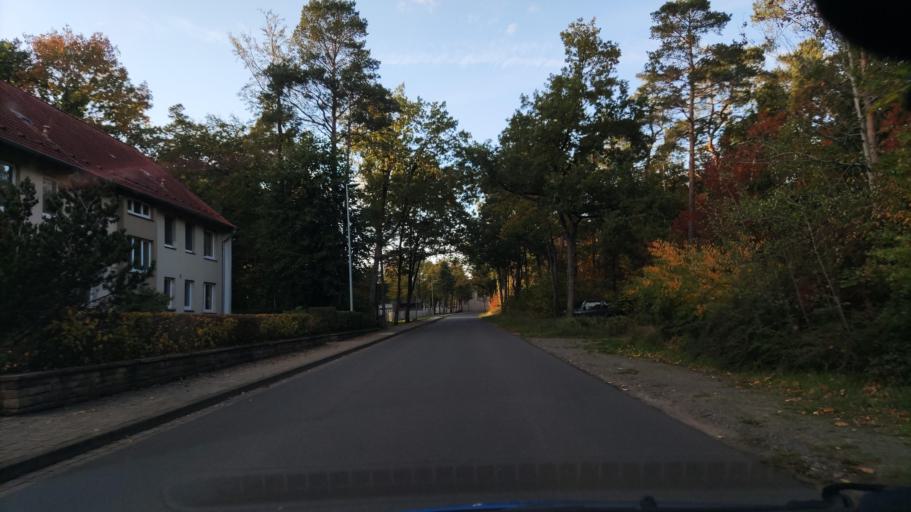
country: DE
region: Lower Saxony
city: Munster
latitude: 52.9792
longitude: 10.0781
